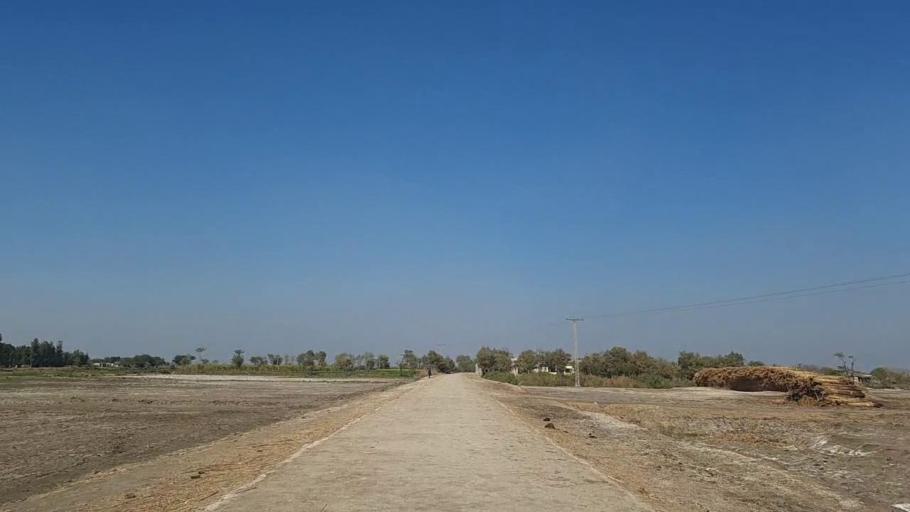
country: PK
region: Sindh
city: Bandhi
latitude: 26.5454
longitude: 68.3270
